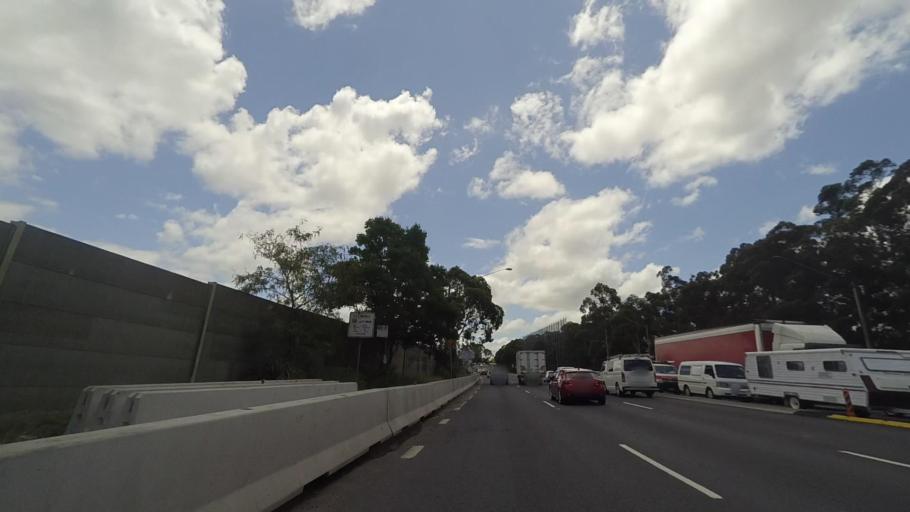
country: AU
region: New South Wales
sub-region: The Hills Shire
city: West Pennant
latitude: -33.7574
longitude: 151.0486
